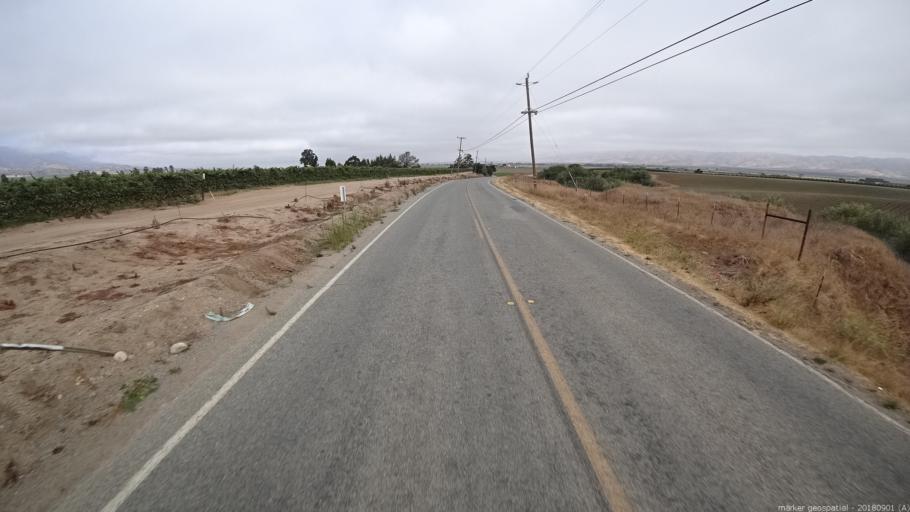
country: US
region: California
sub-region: Monterey County
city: Soledad
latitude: 36.3698
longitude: -121.3249
